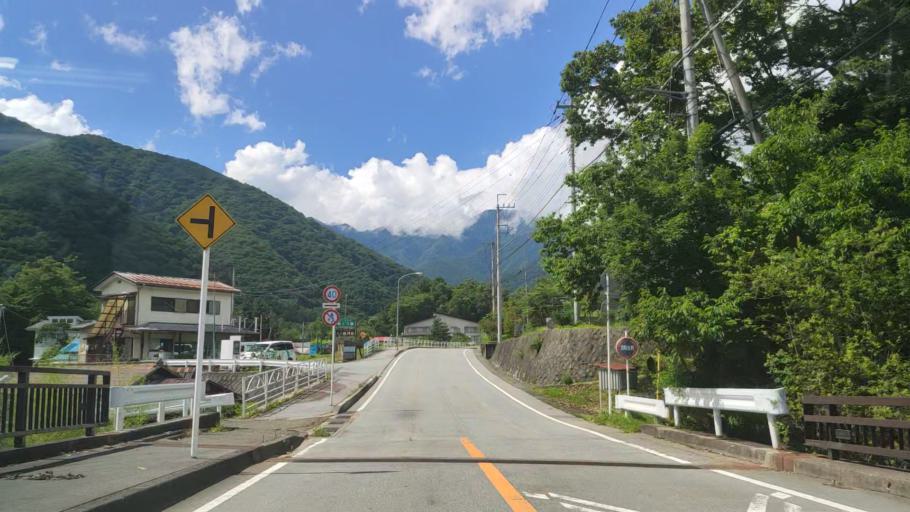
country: JP
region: Yamanashi
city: Enzan
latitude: 35.8497
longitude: 138.7598
